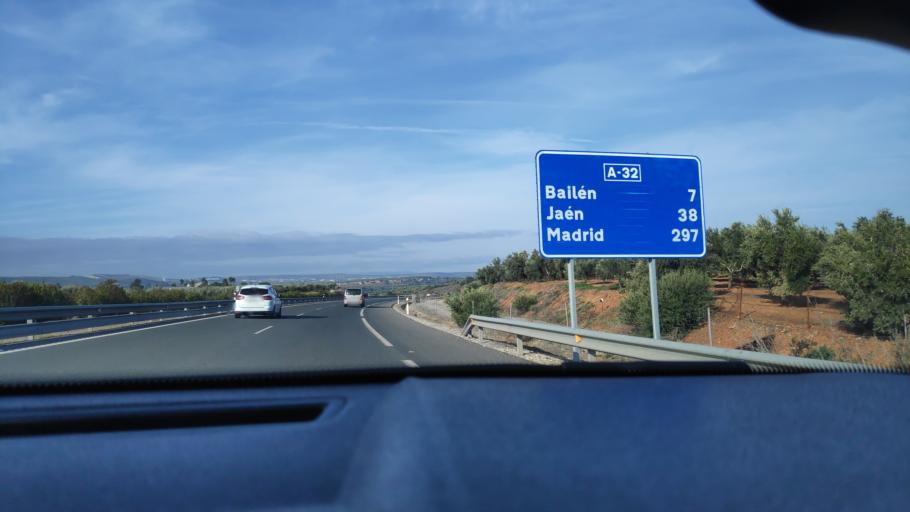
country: ES
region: Andalusia
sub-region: Provincia de Jaen
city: Bailen
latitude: 38.0964
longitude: -3.7076
